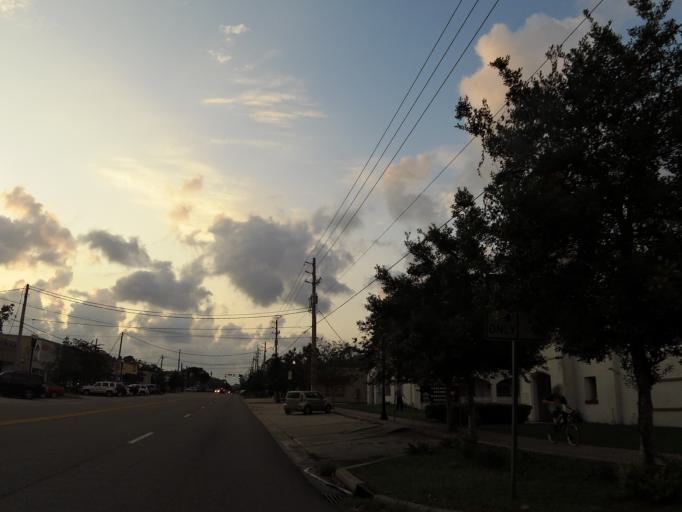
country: US
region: Florida
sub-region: Duval County
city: Jacksonville
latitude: 30.3112
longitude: -81.7168
